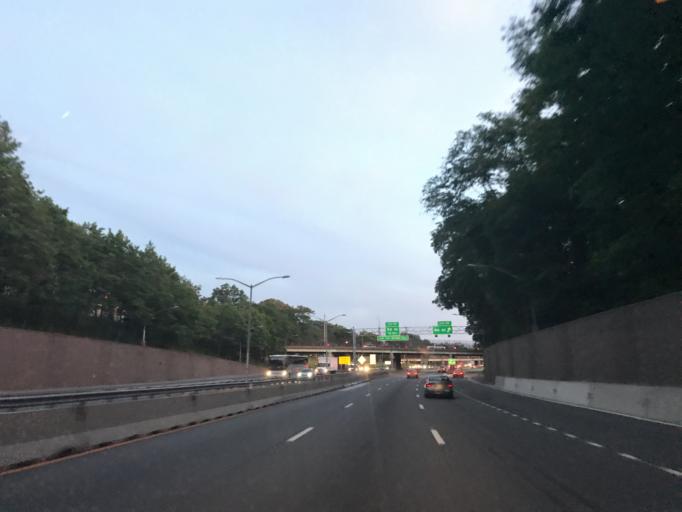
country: US
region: New York
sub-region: Kings County
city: Bensonhurst
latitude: 40.6260
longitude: -74.0187
